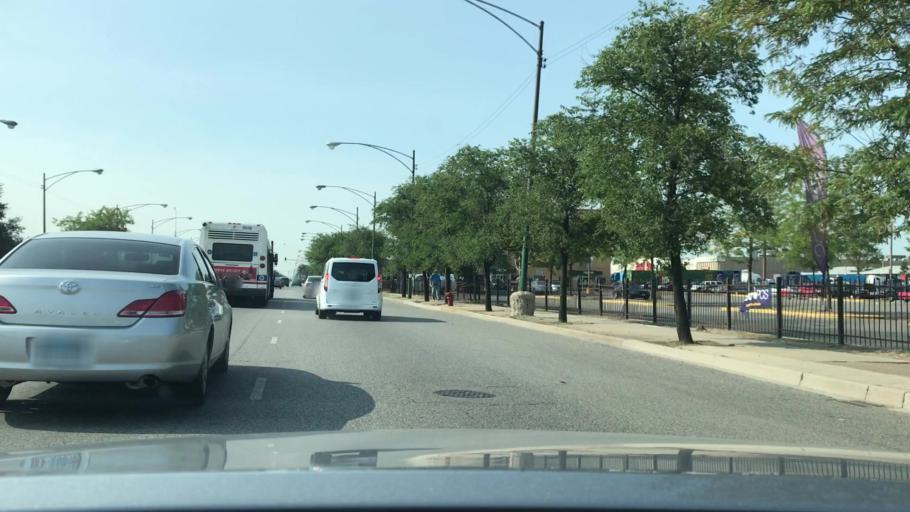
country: US
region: Illinois
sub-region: Cook County
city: Cicero
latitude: 41.7974
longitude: -87.7250
